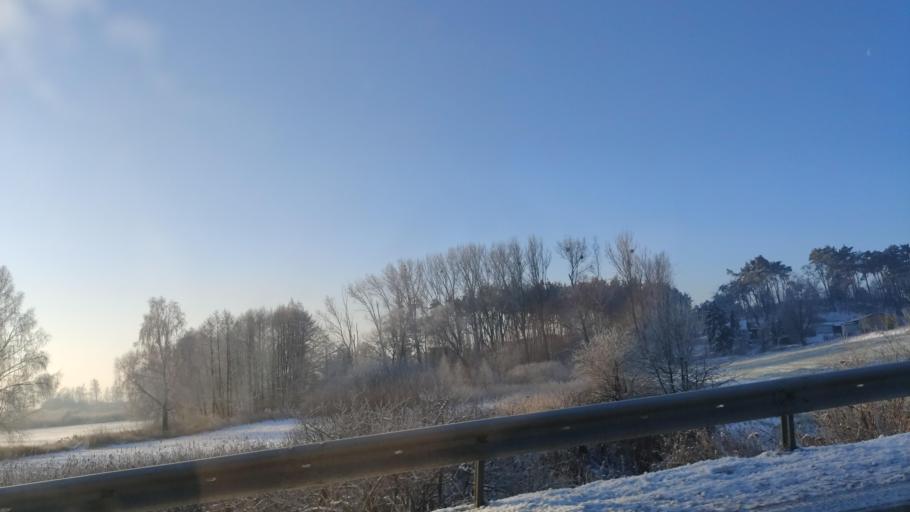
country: PL
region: Kujawsko-Pomorskie
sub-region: Powiat zninski
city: Barcin
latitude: 52.8759
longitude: 17.8938
